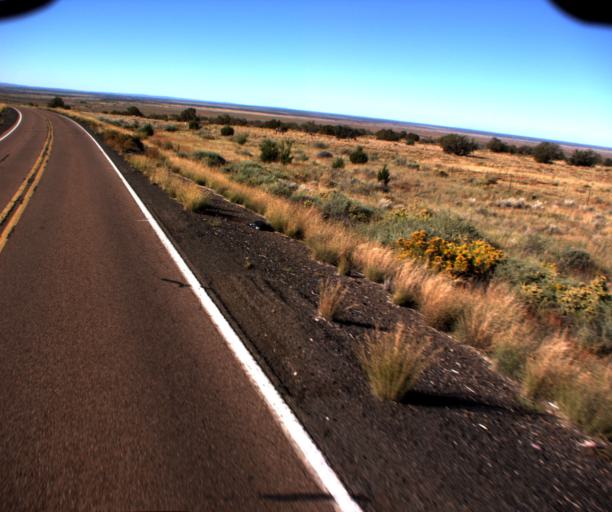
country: US
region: Arizona
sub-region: Navajo County
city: Snowflake
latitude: 34.6407
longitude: -110.3573
